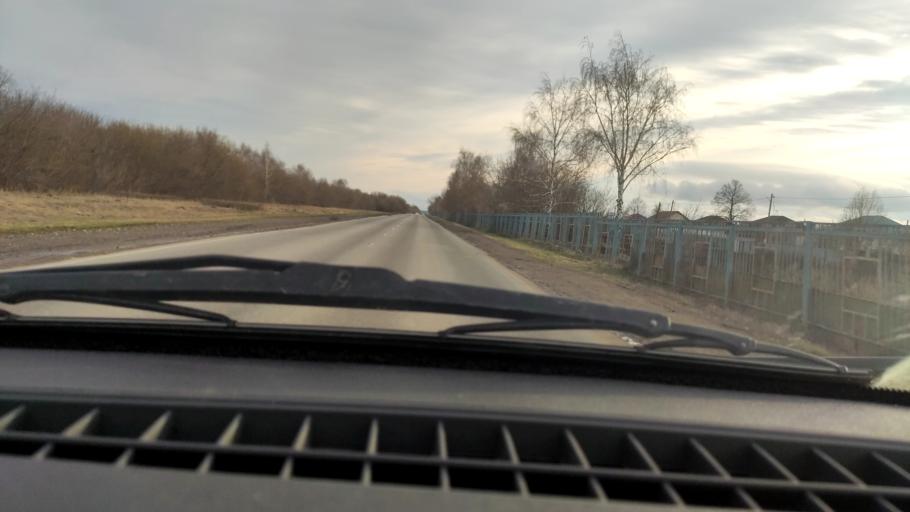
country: RU
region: Bashkortostan
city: Davlekanovo
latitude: 54.3003
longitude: 55.1317
